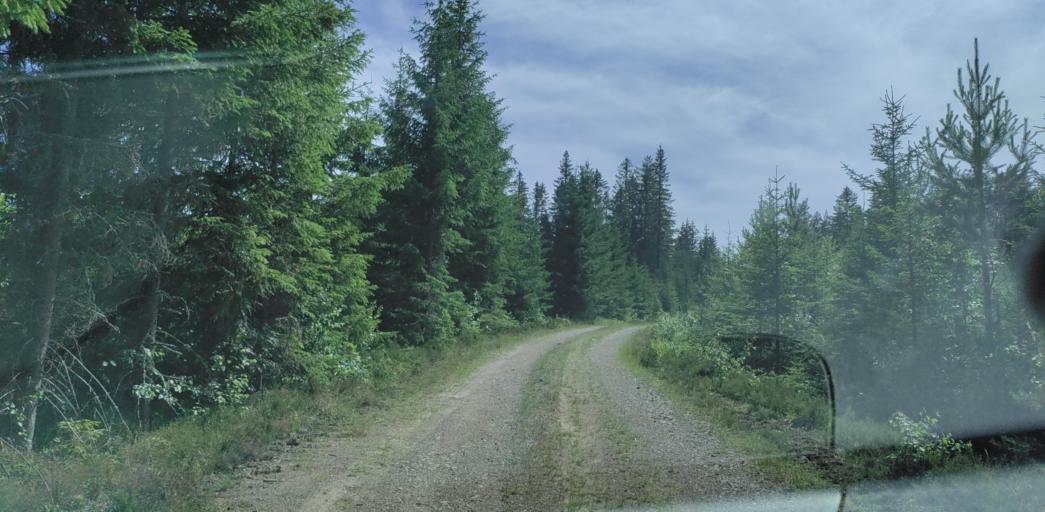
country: SE
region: Vaermland
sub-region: Hagfors Kommun
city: Ekshaerad
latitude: 60.0919
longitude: 13.3766
